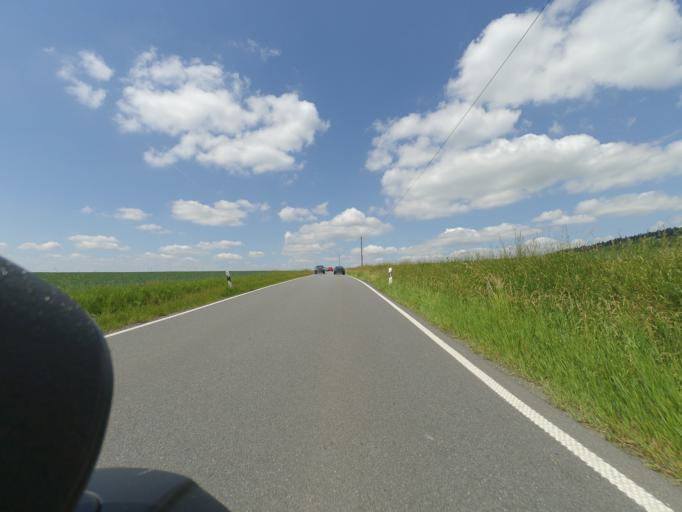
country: DE
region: Saxony
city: Stadt Wehlen
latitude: 50.9879
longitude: 14.0648
